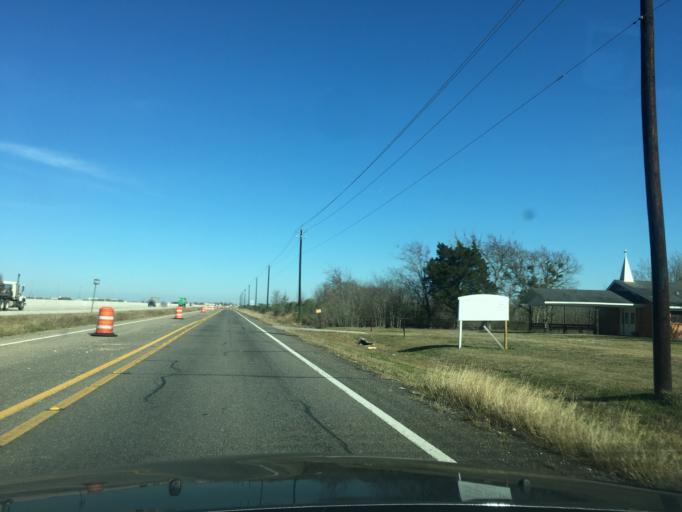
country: US
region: Texas
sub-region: Wharton County
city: East Bernard
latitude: 29.4565
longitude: -95.9823
